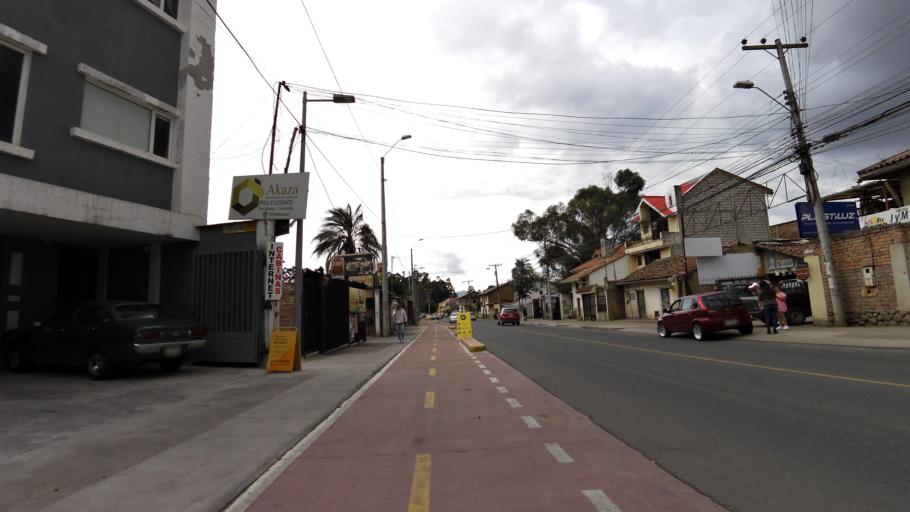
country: EC
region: Azuay
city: Cuenca
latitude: -2.9079
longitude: -79.0290
